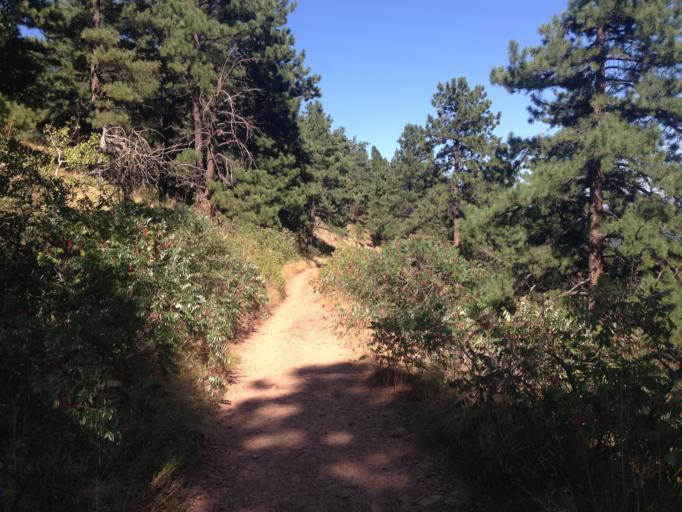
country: US
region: Colorado
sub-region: Boulder County
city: Boulder
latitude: 39.9846
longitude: -105.2875
